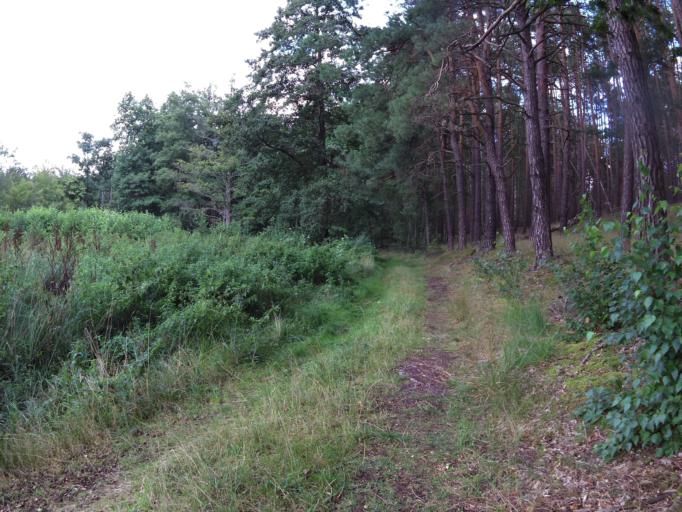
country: DE
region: Brandenburg
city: Munchehofe
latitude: 52.1863
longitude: 13.9006
